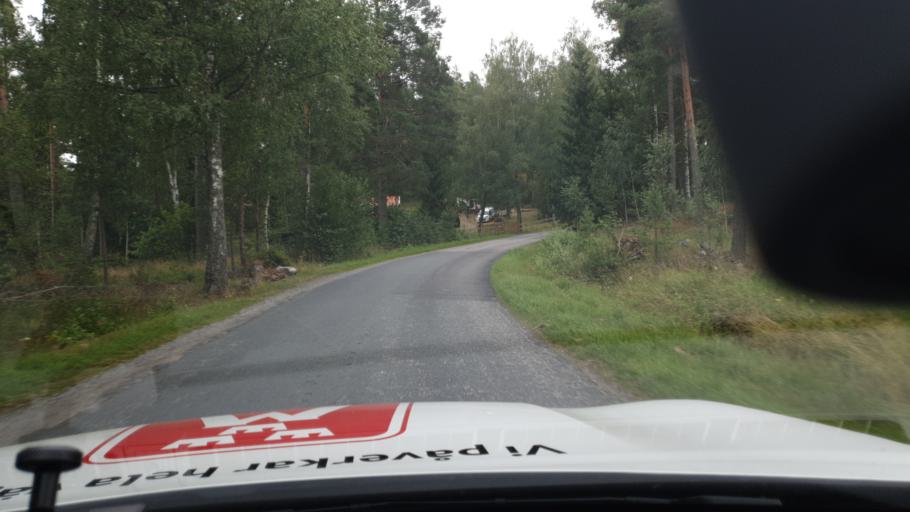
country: SE
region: Soedermanland
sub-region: Strangnas Kommun
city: Mariefred
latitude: 59.1765
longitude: 17.1709
